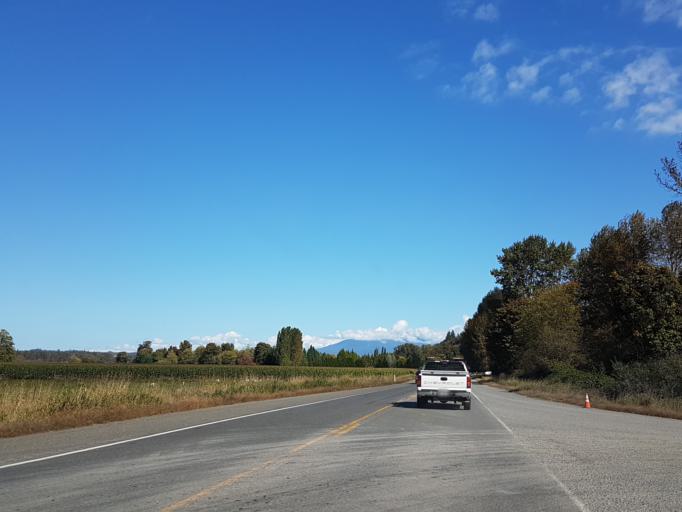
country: US
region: Washington
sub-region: Snohomish County
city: Monroe
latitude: 47.8195
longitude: -121.9770
